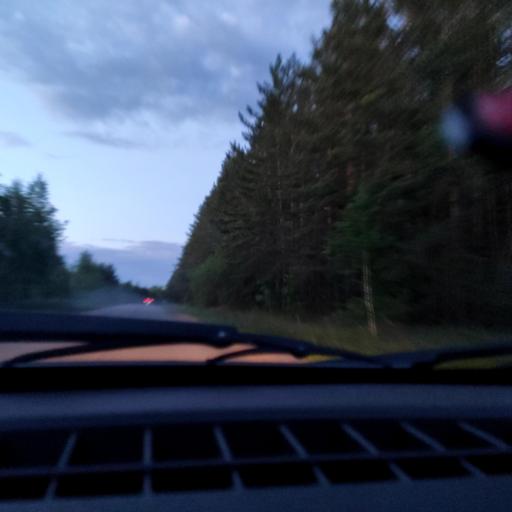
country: RU
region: Bashkortostan
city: Avdon
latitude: 54.6460
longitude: 55.5737
